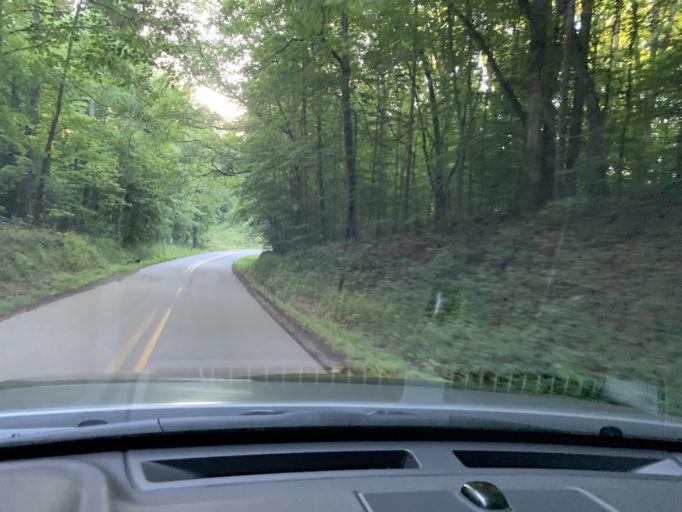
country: US
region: Georgia
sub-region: Bartow County
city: Rydal
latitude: 34.2449
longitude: -84.6736
